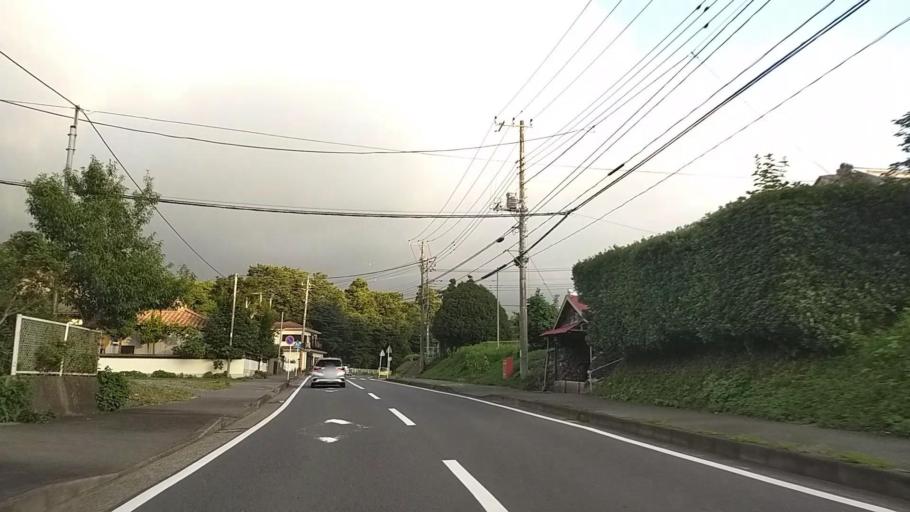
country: JP
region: Kanagawa
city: Atsugi
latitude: 35.4754
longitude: 139.2839
